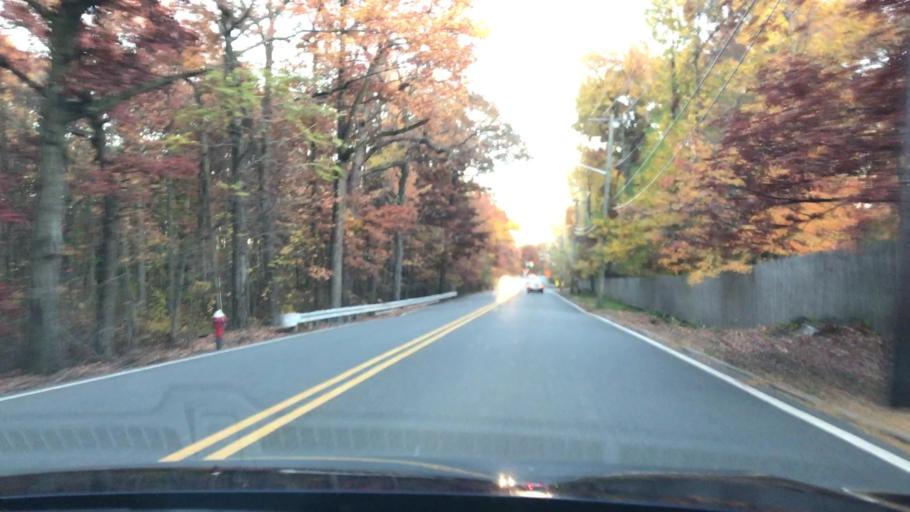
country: US
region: New Jersey
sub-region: Bergen County
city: Englewood Cliffs
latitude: 40.9049
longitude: -73.9407
